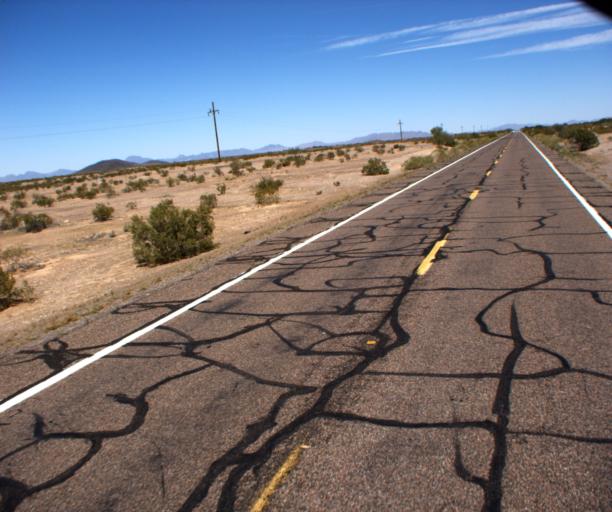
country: US
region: Arizona
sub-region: Maricopa County
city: Gila Bend
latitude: 32.7876
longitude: -112.8065
